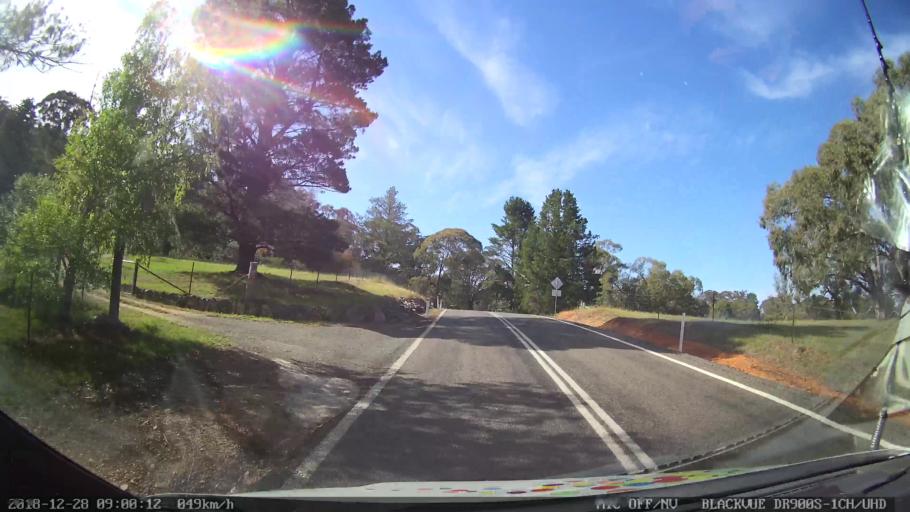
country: AU
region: New South Wales
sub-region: Upper Lachlan Shire
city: Crookwell
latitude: -34.1364
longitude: 149.3344
